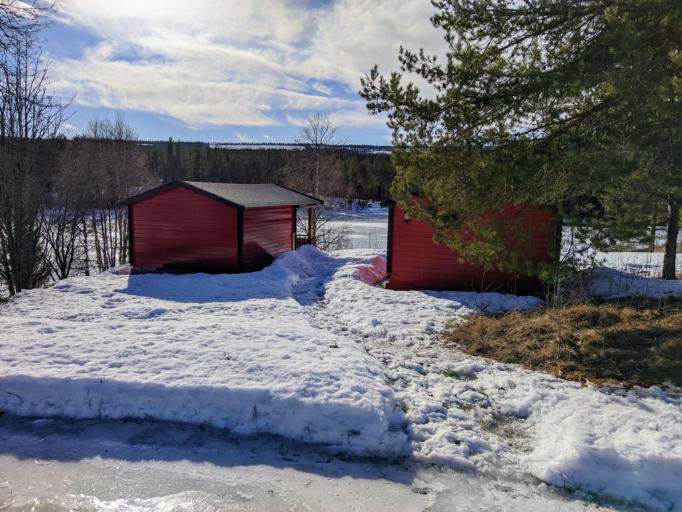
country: NO
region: Hedmark
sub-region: Trysil
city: Innbygda
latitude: 61.2914
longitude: 12.2836
